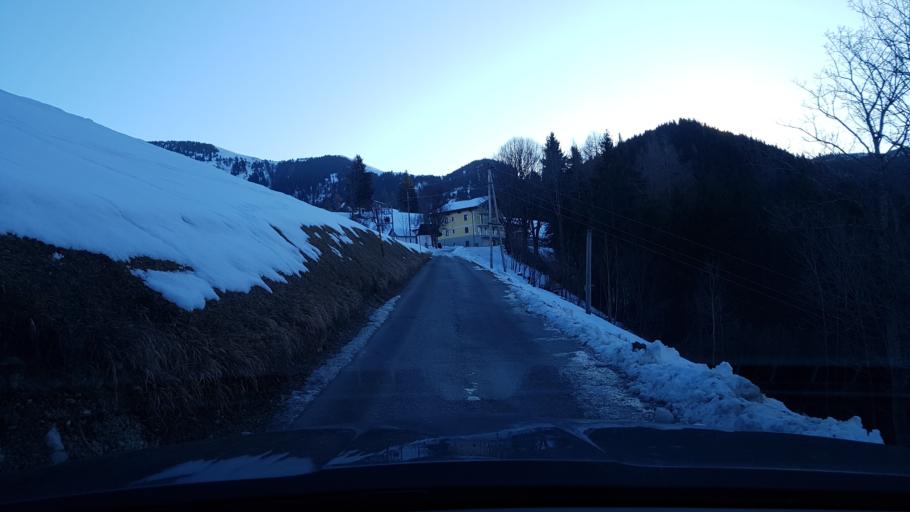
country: AT
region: Salzburg
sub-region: Politischer Bezirk Hallein
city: Scheffau am Tennengebirge
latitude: 47.6478
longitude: 13.2345
